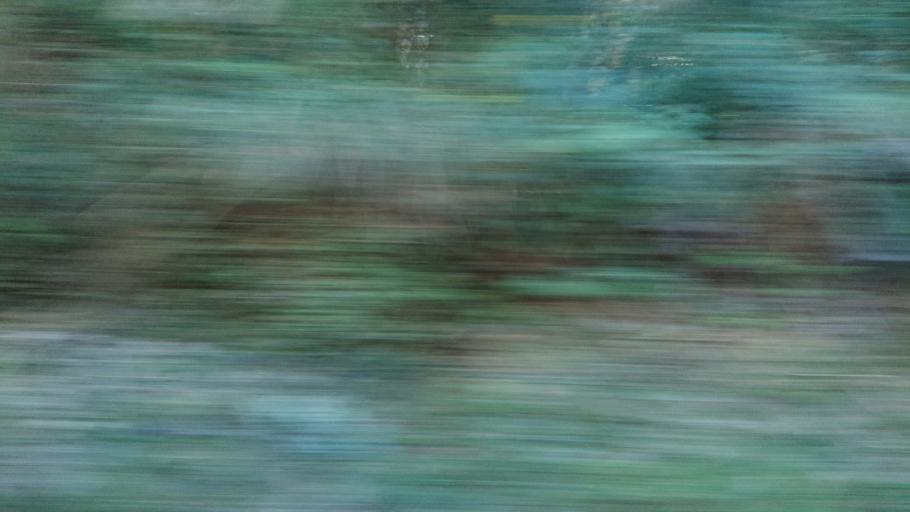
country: TW
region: Taiwan
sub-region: Hualien
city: Hualian
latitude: 24.3715
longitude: 121.3398
